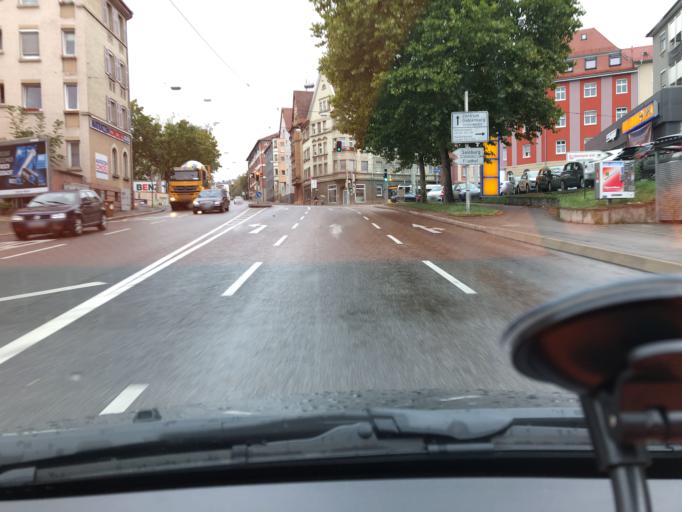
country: DE
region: Baden-Wuerttemberg
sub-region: Regierungsbezirk Stuttgart
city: Stuttgart-Ost
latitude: 48.7848
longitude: 9.2138
